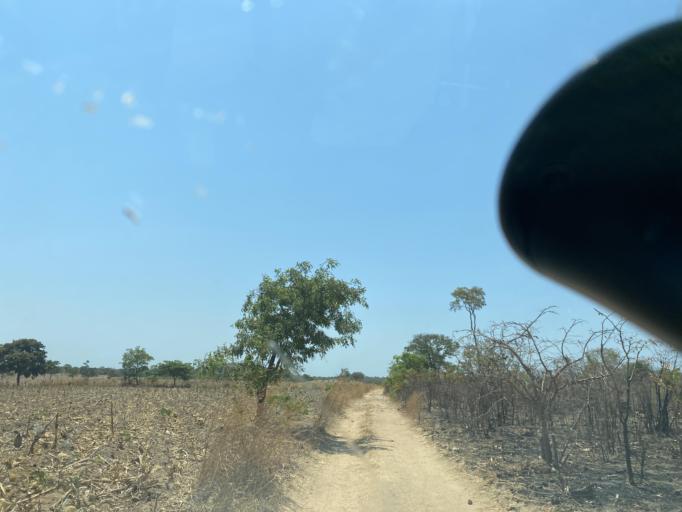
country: ZM
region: Lusaka
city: Chongwe
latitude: -15.4319
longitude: 29.1913
